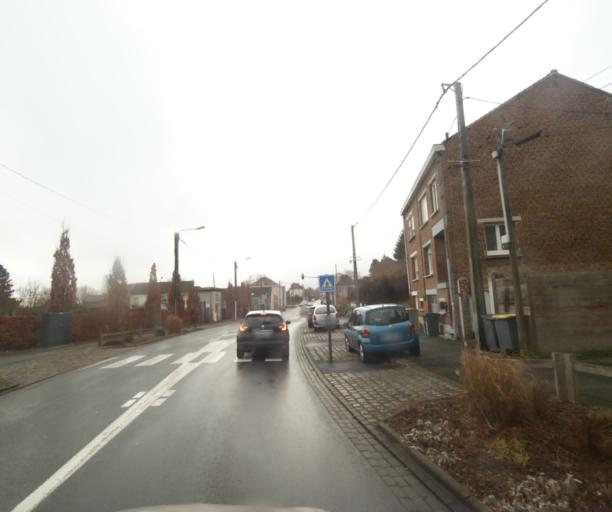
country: FR
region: Nord-Pas-de-Calais
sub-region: Departement du Nord
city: Aulnoy-lez-Valenciennes
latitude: 50.3296
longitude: 3.5230
